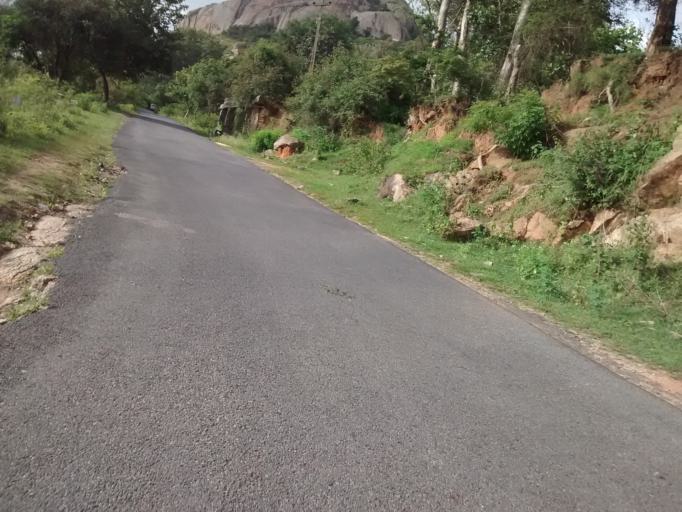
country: IN
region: Karnataka
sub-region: Tumkur
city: Tumkur
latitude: 13.3753
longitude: 77.2114
